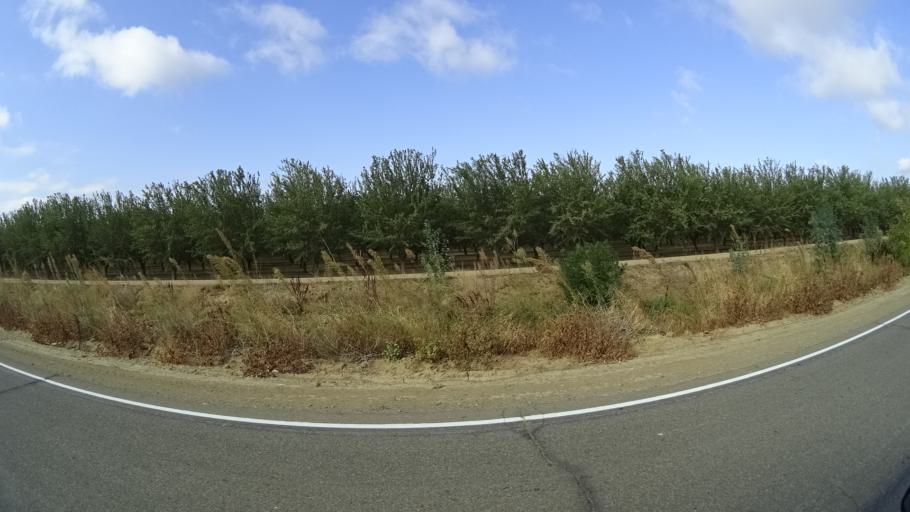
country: US
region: California
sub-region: Yolo County
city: Esparto
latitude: 38.7540
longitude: -122.0072
